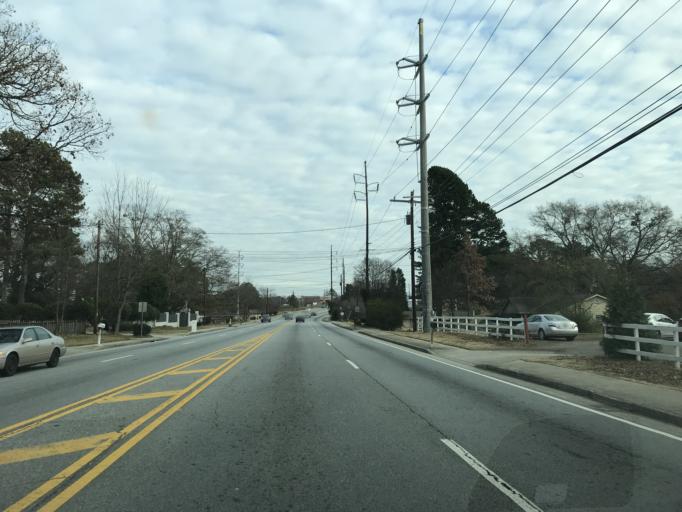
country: US
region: Georgia
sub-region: DeKalb County
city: Doraville
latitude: 33.8822
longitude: -84.2787
